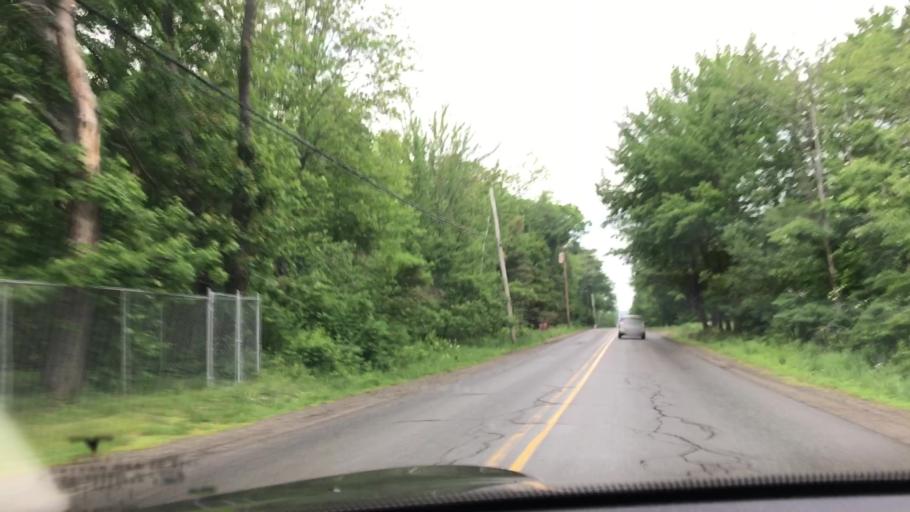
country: US
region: Maine
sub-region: Penobscot County
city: Orono
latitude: 44.8967
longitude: -68.6978
